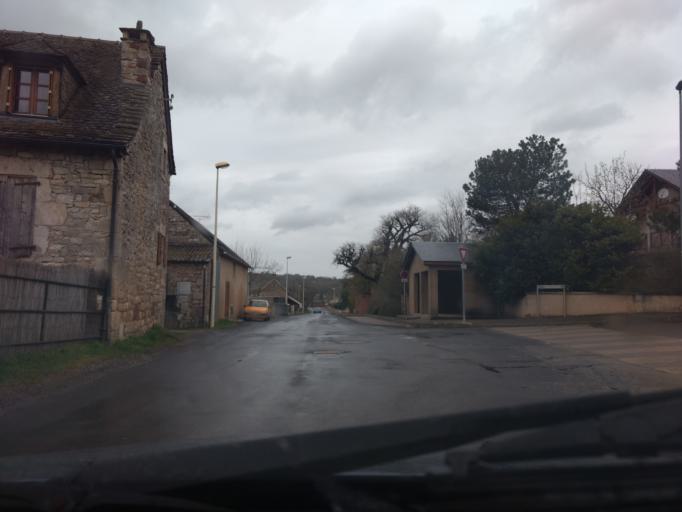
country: FR
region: Midi-Pyrenees
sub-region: Departement de l'Aveyron
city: La Loubiere
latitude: 44.3978
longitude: 2.6978
